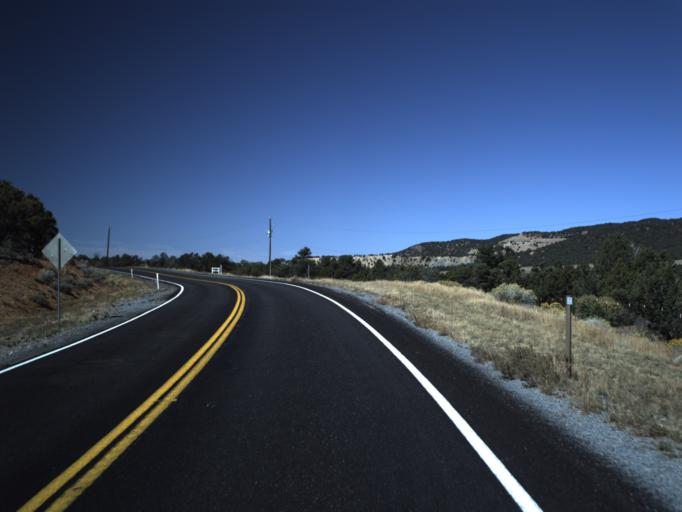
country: US
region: Utah
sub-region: Iron County
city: Cedar City
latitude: 37.6086
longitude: -113.3610
